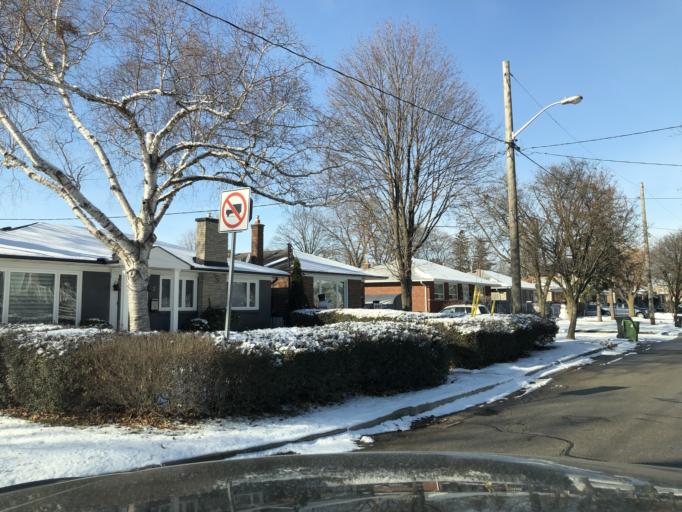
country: CA
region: Ontario
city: Etobicoke
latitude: 43.7079
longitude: -79.5158
